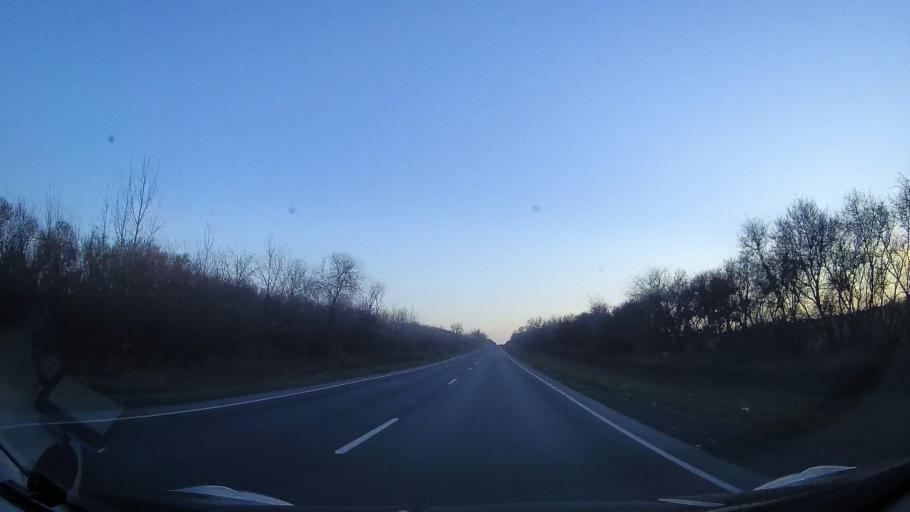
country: RU
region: Rostov
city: Bagayevskaya
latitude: 47.1382
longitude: 40.2766
